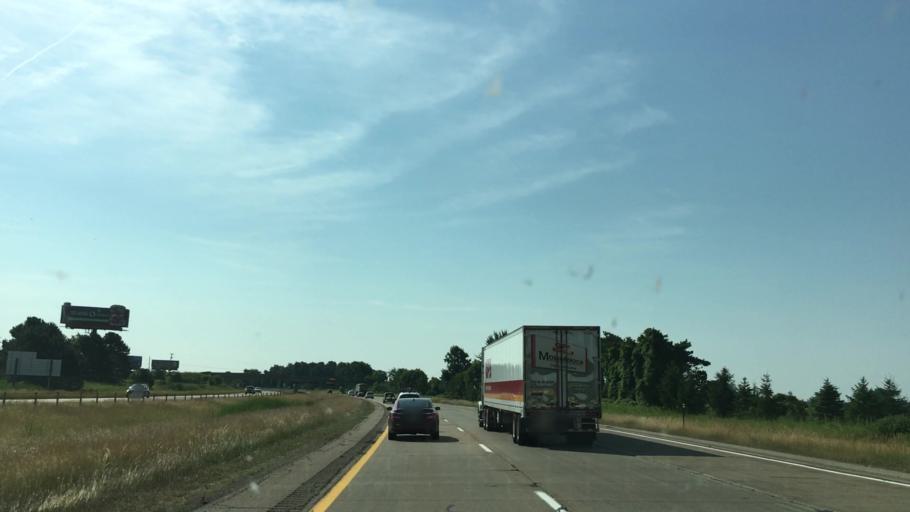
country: US
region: Michigan
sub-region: Ionia County
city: Portland
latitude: 42.8688
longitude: -84.9599
